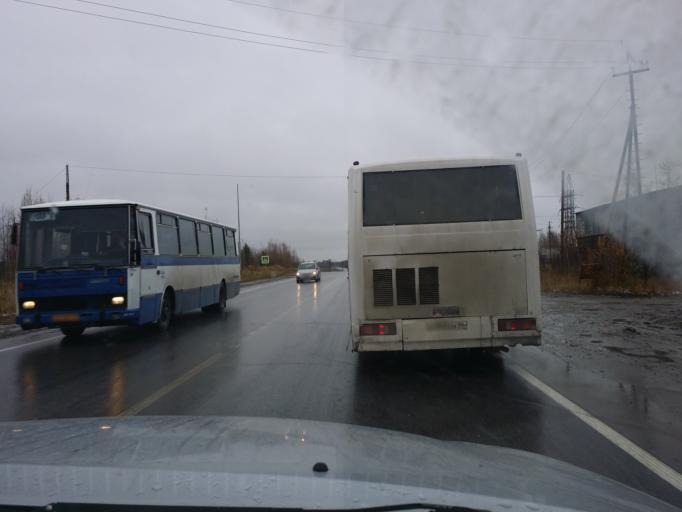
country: RU
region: Khanty-Mansiyskiy Avtonomnyy Okrug
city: Megion
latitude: 61.0536
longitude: 76.1130
